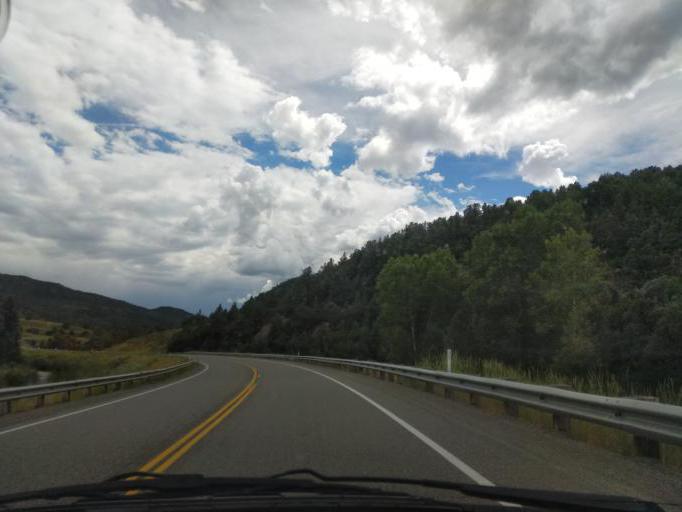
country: US
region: Colorado
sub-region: Delta County
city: Paonia
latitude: 39.0567
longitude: -107.3636
